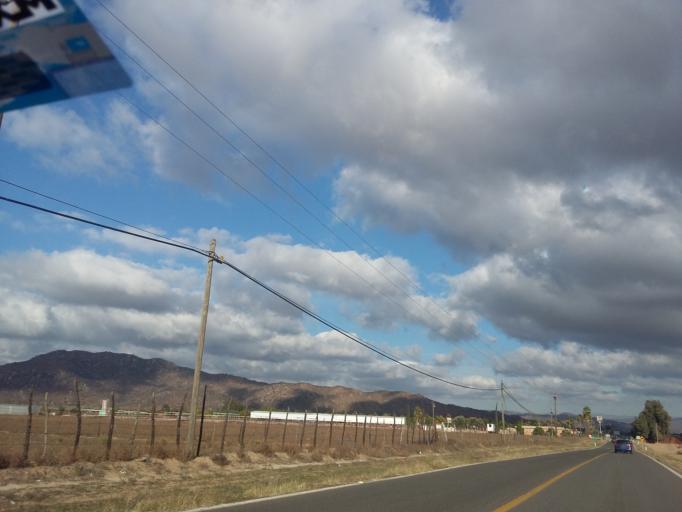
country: MX
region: Baja California
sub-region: Ensenada
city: Rancho Verde
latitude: 32.0837
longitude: -116.6033
